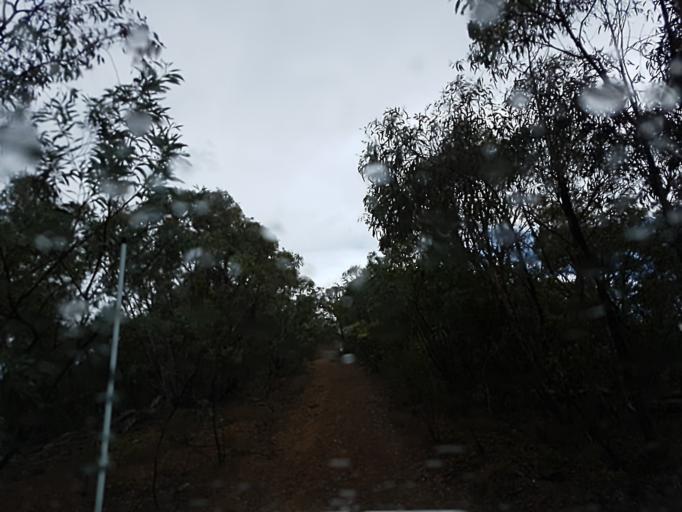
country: AU
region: New South Wales
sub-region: Snowy River
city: Jindabyne
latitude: -36.9067
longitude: 148.3405
